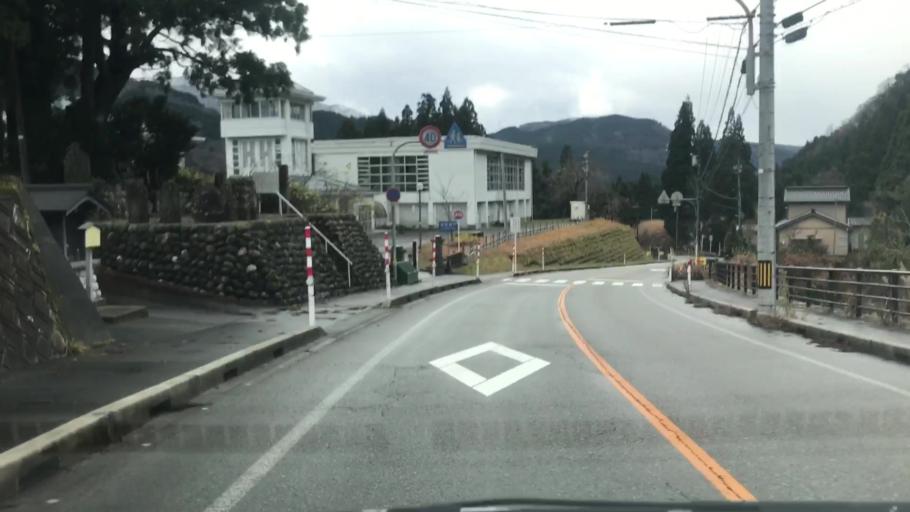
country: JP
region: Toyama
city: Kamiichi
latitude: 36.5782
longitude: 137.3850
